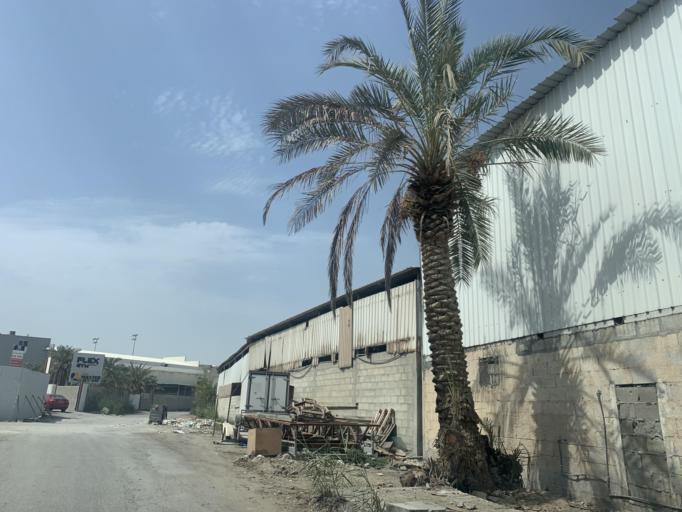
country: BH
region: Central Governorate
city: Madinat Hamad
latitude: 26.1385
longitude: 50.4865
